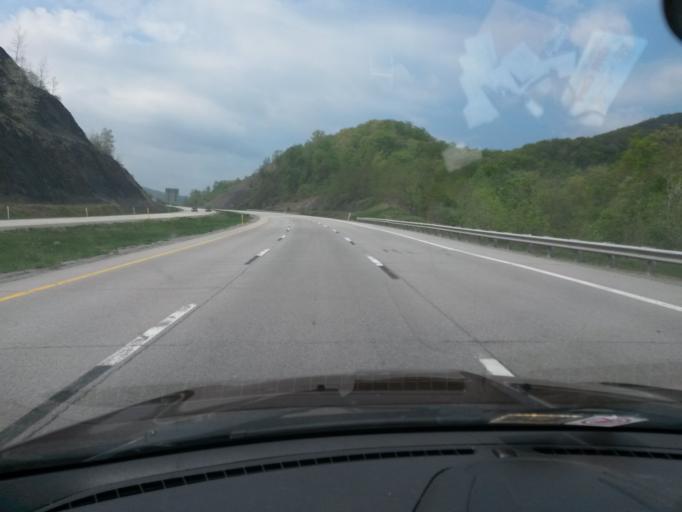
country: US
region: West Virginia
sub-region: Randolph County
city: Elkins
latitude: 38.9470
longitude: -79.8870
